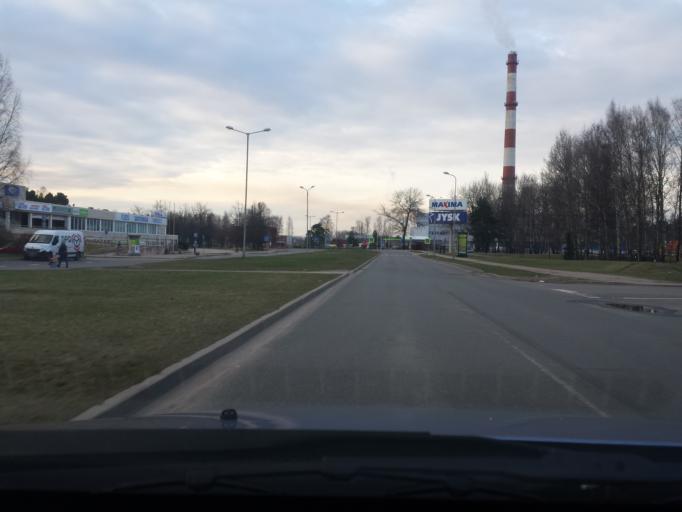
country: LV
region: Marupe
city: Marupe
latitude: 56.9591
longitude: 24.0352
